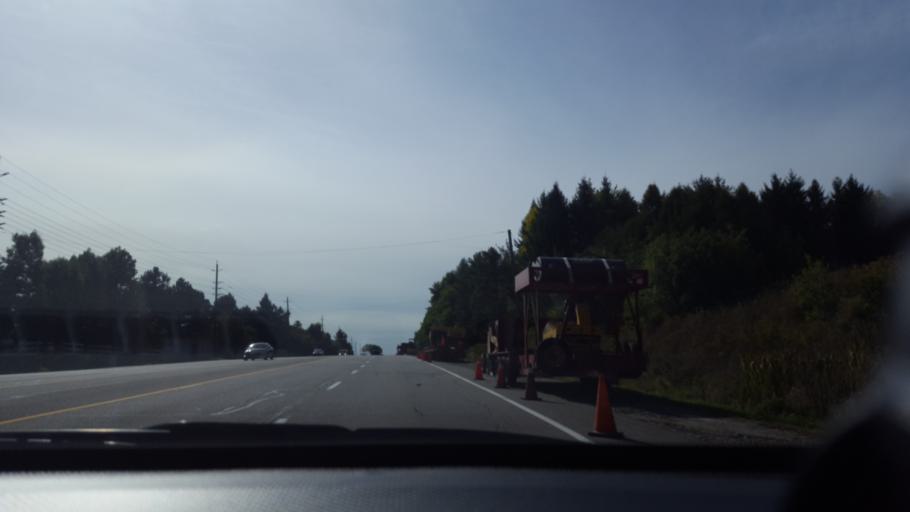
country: CA
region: Ontario
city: Newmarket
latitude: 43.9931
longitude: -79.4940
